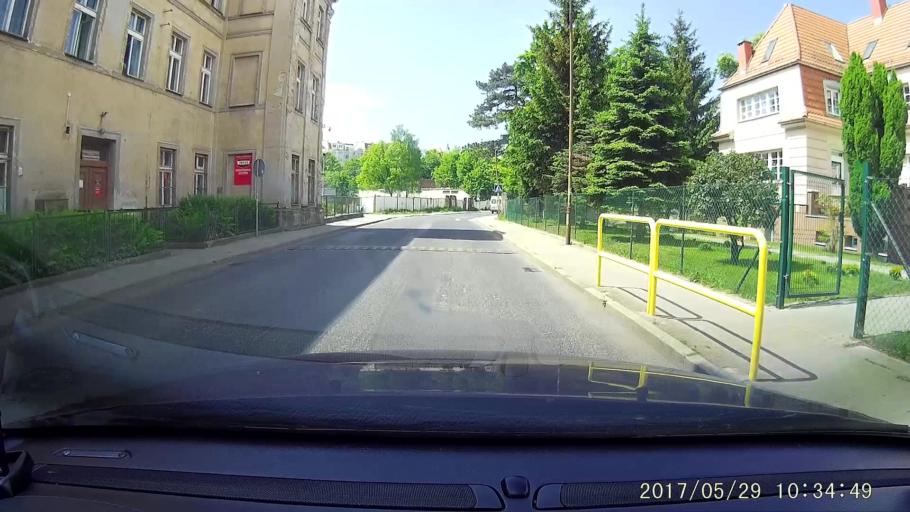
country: PL
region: Lower Silesian Voivodeship
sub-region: Jelenia Gora
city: Jelenia Gora
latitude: 50.9050
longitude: 15.7416
